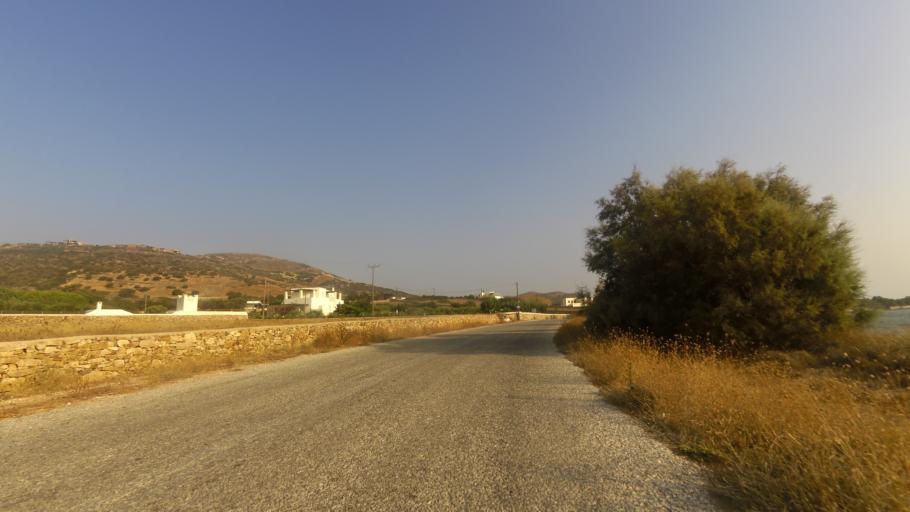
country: GR
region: South Aegean
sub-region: Nomos Kykladon
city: Antiparos
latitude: 37.0133
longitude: 25.0752
